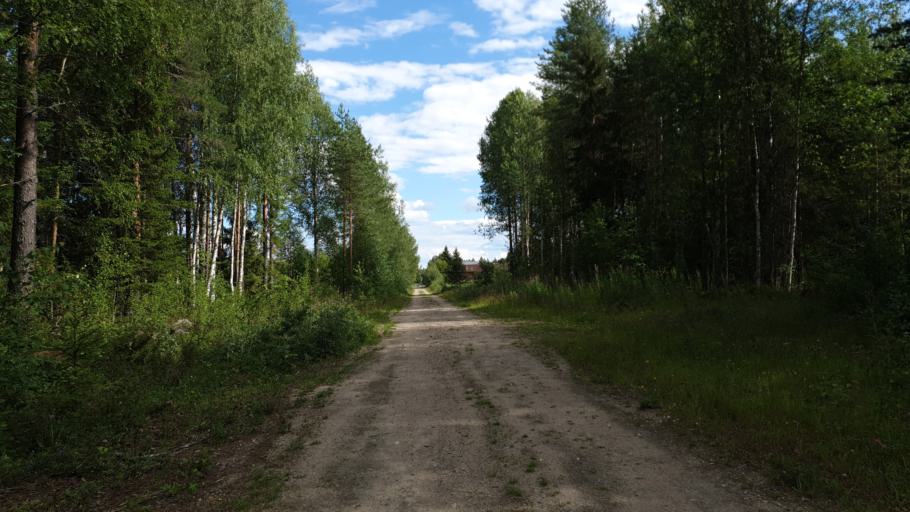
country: FI
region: Kainuu
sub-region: Kehys-Kainuu
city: Kuhmo
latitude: 64.1142
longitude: 29.5197
